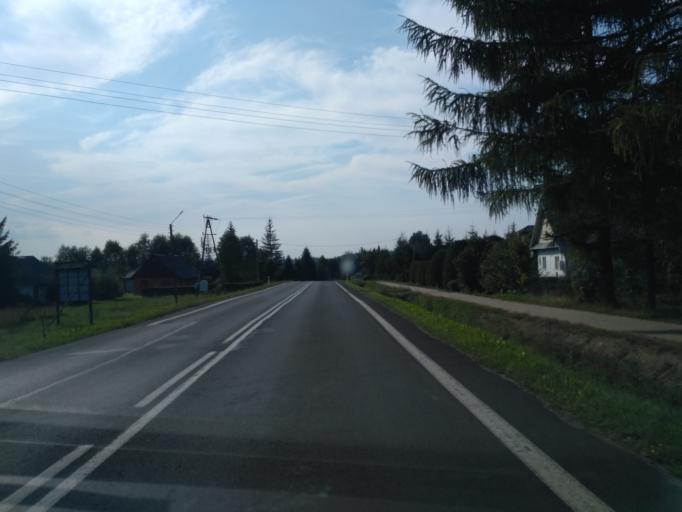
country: PL
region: Subcarpathian Voivodeship
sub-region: Powiat bieszczadzki
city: Ustrzyki Dolne
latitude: 49.4263
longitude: 22.5454
